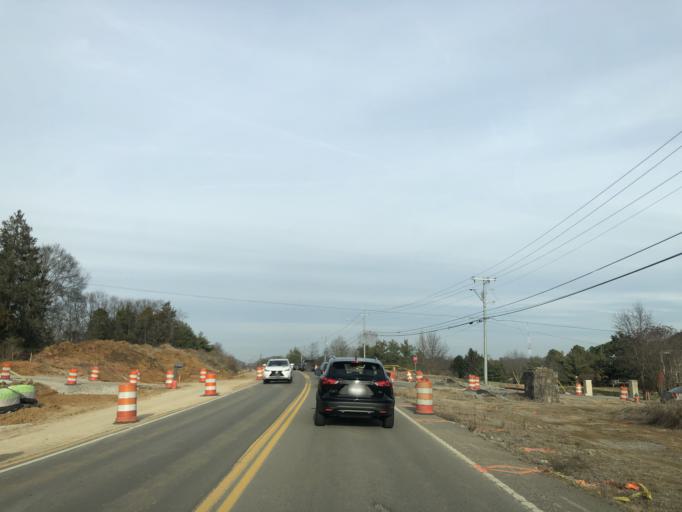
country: US
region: Tennessee
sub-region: Williamson County
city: Brentwood Estates
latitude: 35.9846
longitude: -86.8184
